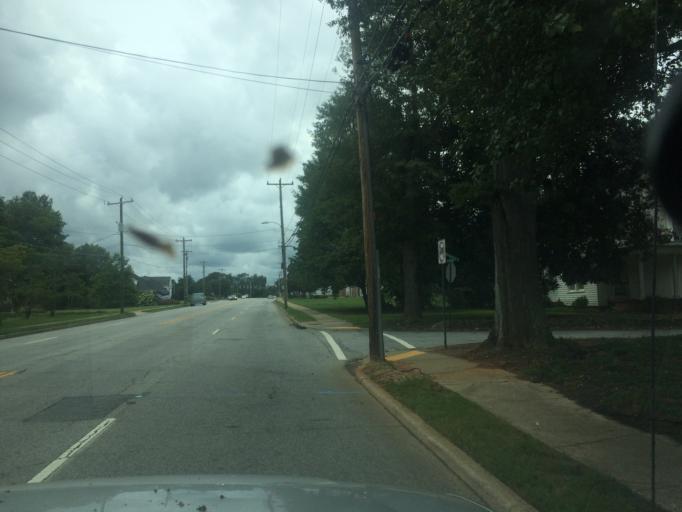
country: US
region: South Carolina
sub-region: Greenville County
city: Greer
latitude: 34.9423
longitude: -82.2446
